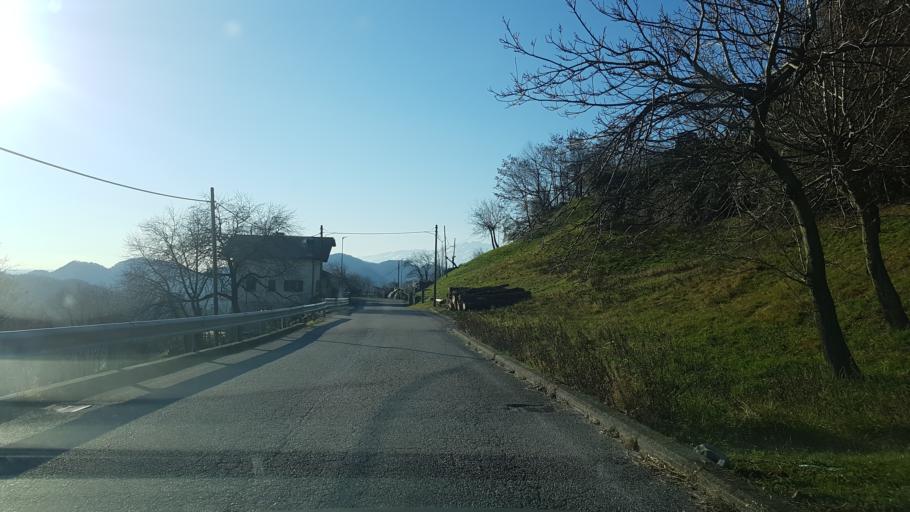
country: IT
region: Friuli Venezia Giulia
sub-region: Provincia di Udine
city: Forgaria nel Friuli
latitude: 46.2259
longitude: 12.9828
